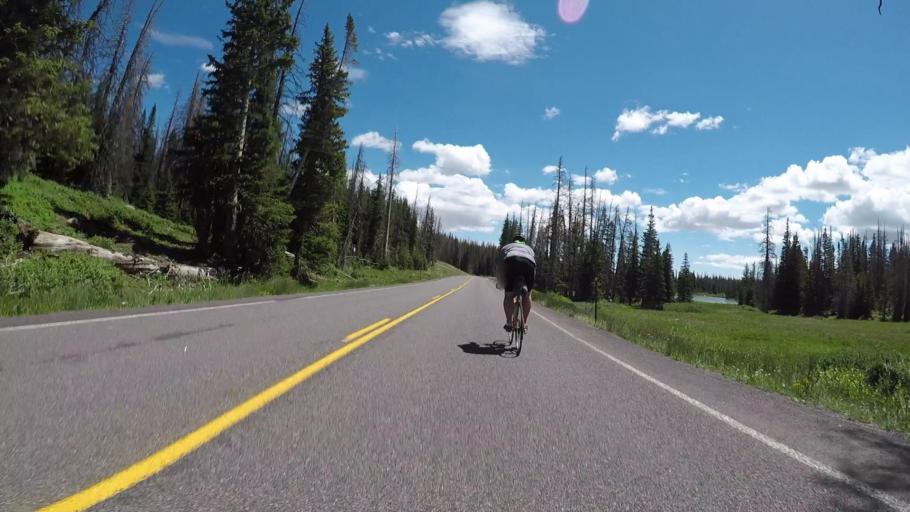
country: US
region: Wyoming
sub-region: Carbon County
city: Saratoga
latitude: 41.3520
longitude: -106.2676
